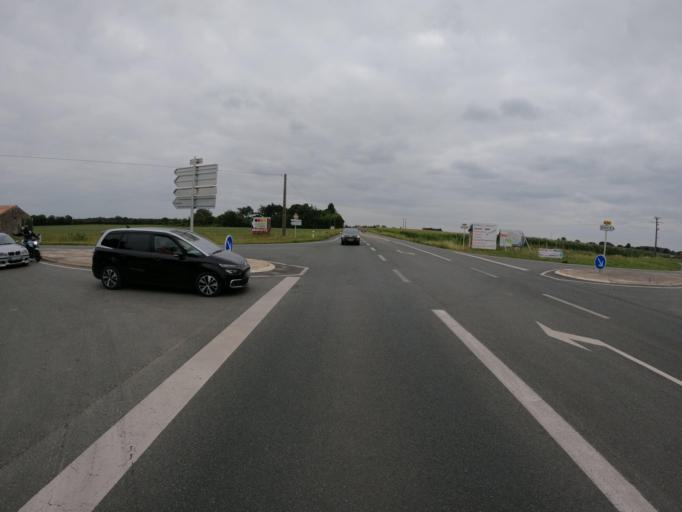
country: FR
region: Pays de la Loire
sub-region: Departement de la Vendee
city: Saint-Hilaire-des-Loges
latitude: 46.4064
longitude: -0.6786
